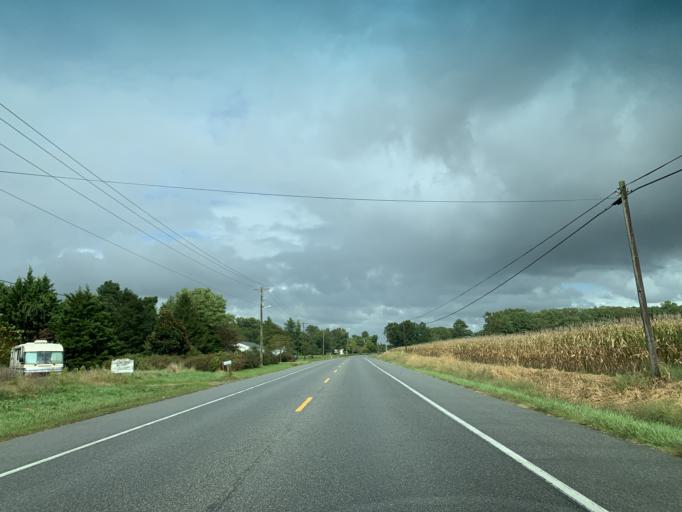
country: US
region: Maryland
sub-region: Caroline County
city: Ridgely
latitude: 38.9627
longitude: -75.8875
